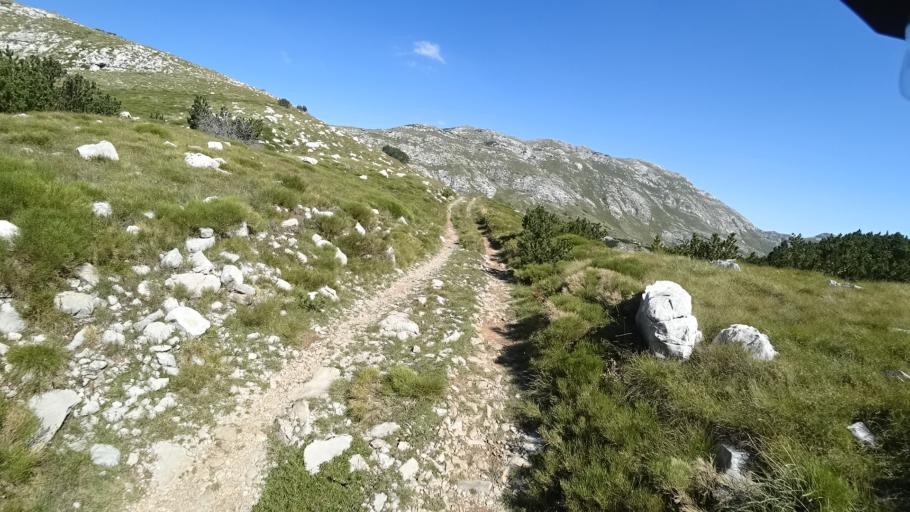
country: HR
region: Splitsko-Dalmatinska
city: Hrvace
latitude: 43.9372
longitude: 16.5749
